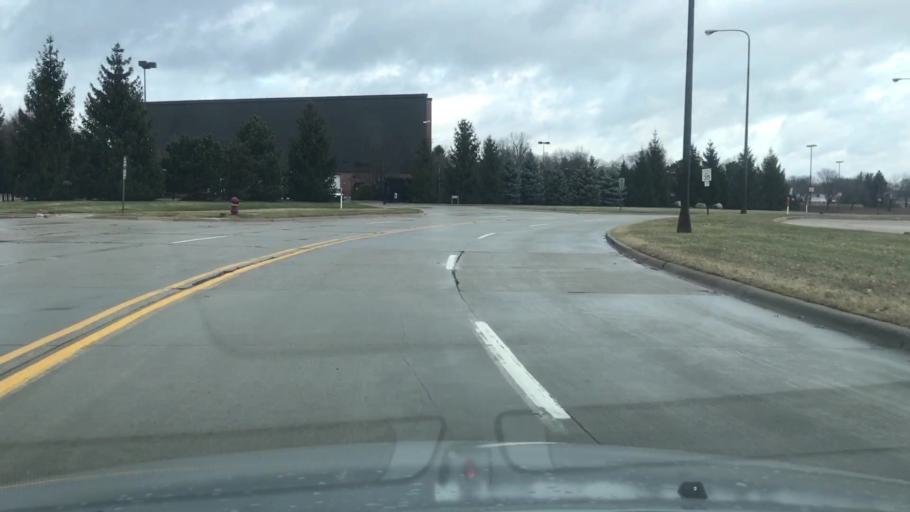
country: US
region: Michigan
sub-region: Oakland County
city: Birmingham
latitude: 42.5636
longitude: -83.1919
